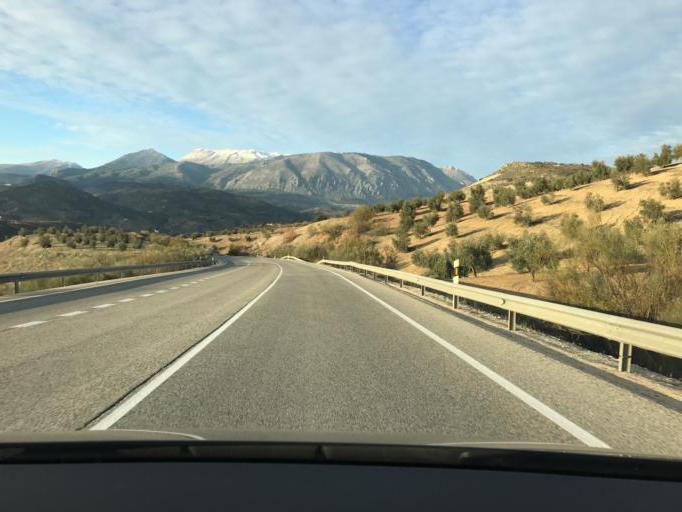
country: ES
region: Andalusia
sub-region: Provincia de Jaen
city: Huelma
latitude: 37.6374
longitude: -3.4107
